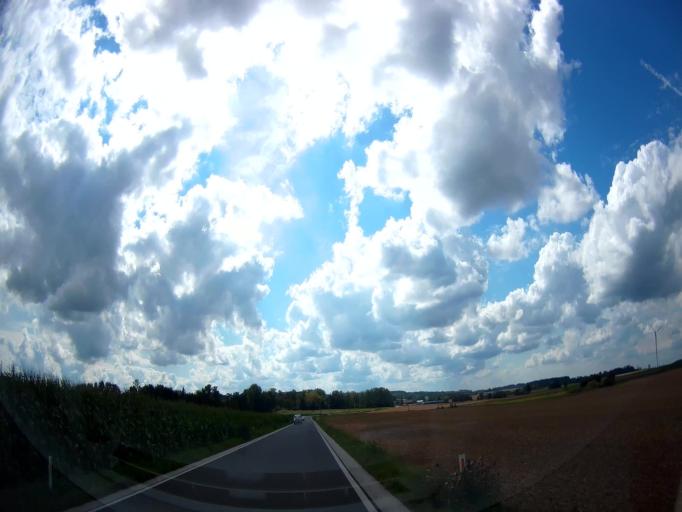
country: BE
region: Wallonia
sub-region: Province de Namur
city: Ohey
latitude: 50.4043
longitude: 5.1168
